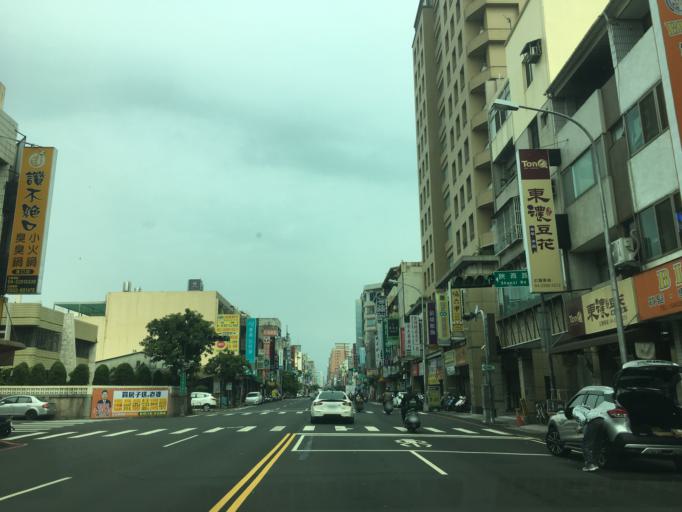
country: TW
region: Taiwan
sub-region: Taichung City
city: Taichung
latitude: 24.1668
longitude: 120.6679
